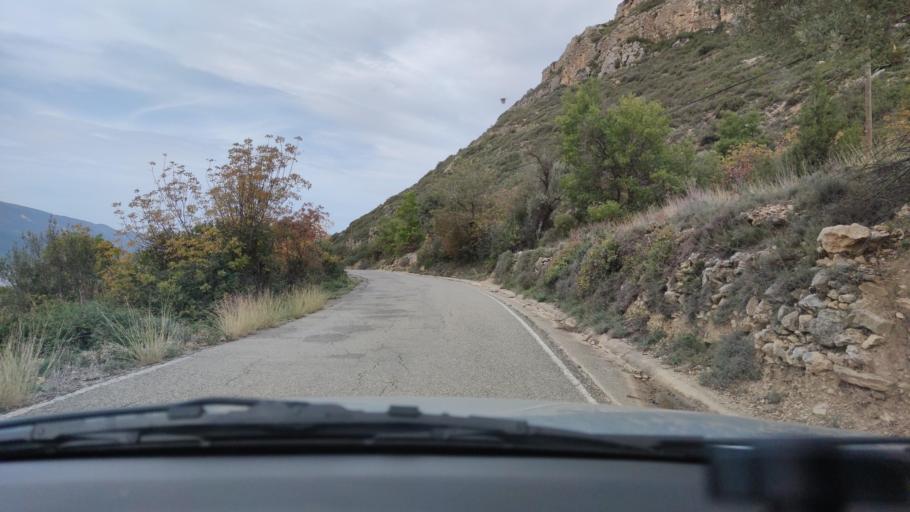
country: ES
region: Catalonia
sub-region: Provincia de Lleida
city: Llimiana
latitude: 42.0680
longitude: 0.9248
